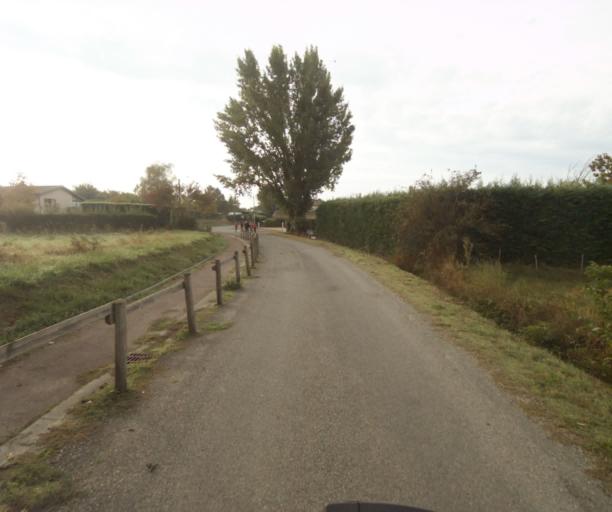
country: FR
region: Midi-Pyrenees
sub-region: Departement du Tarn-et-Garonne
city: Montech
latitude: 43.9662
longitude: 1.2251
